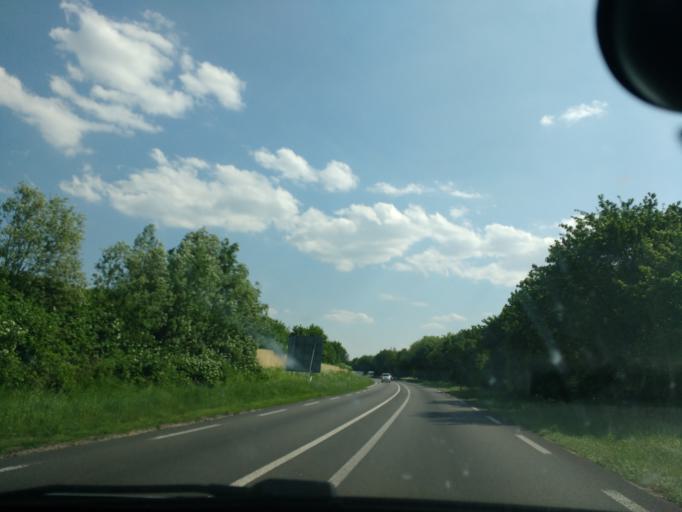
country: NL
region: Utrecht
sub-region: Gemeente Rhenen
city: Rhenen
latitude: 51.9339
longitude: 5.5632
